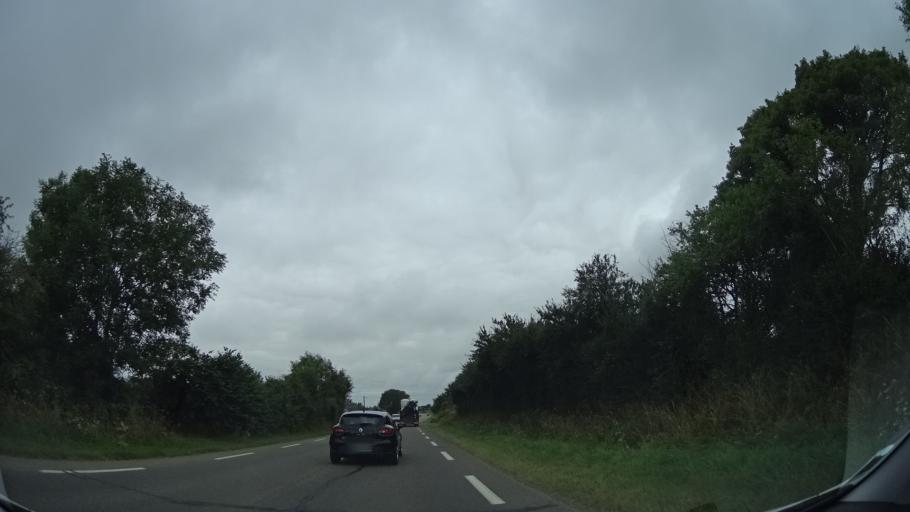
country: FR
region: Lower Normandy
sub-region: Departement de la Manche
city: Portbail
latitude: 49.3575
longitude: -1.6849
